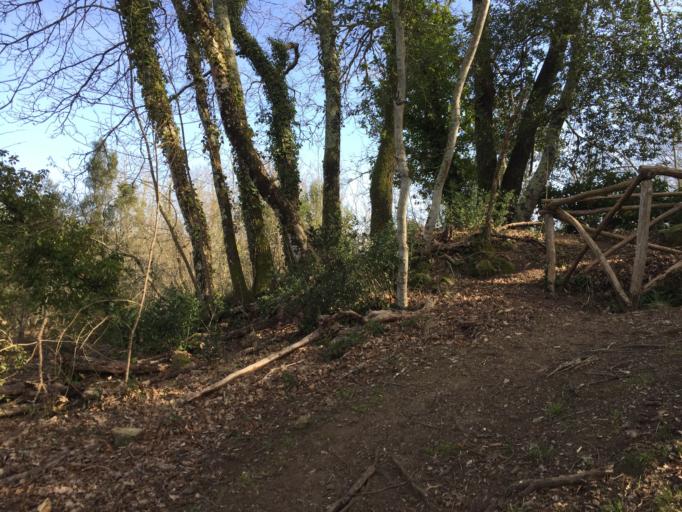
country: IT
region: Latium
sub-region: Provincia di Viterbo
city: Calcata Nuova
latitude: 42.2127
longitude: 12.4199
